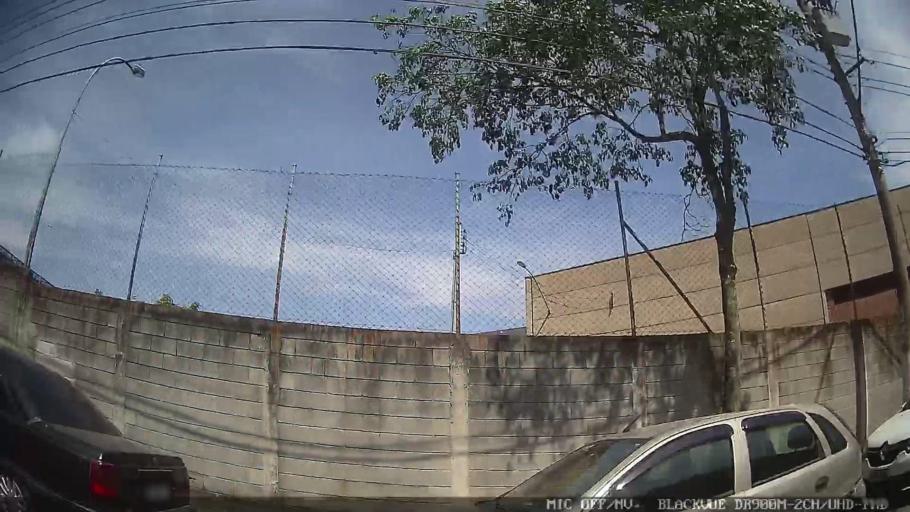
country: BR
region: Sao Paulo
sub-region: Poa
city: Poa
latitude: -23.5231
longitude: -46.3350
